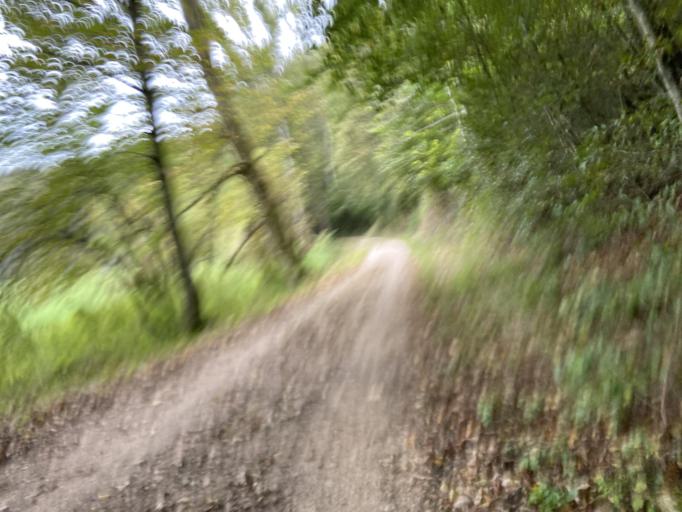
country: DE
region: Baden-Wuerttemberg
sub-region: Tuebingen Region
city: Sigmaringen
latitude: 48.1069
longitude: 9.2271
